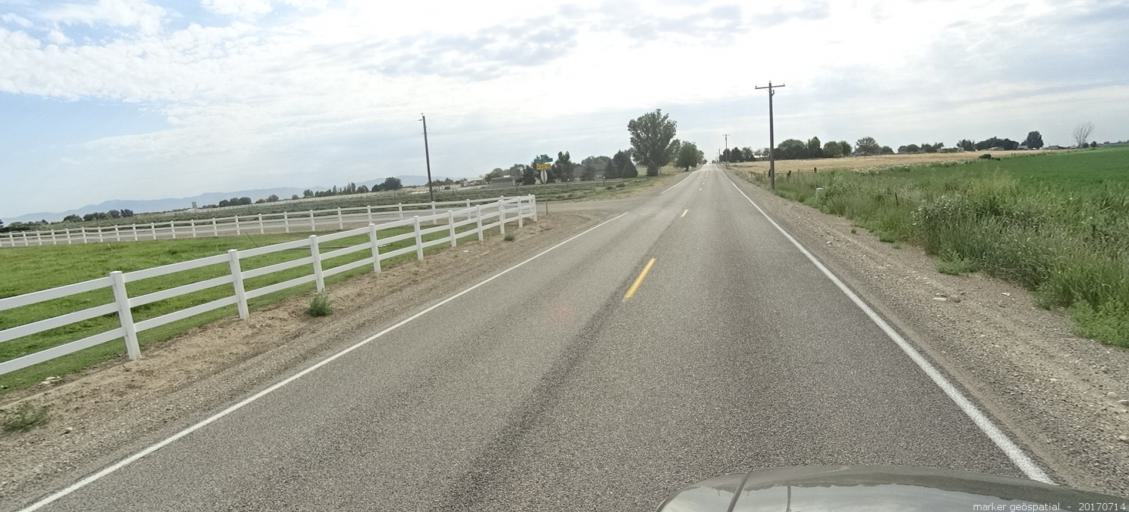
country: US
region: Idaho
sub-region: Ada County
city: Kuna
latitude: 43.4737
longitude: -116.3622
